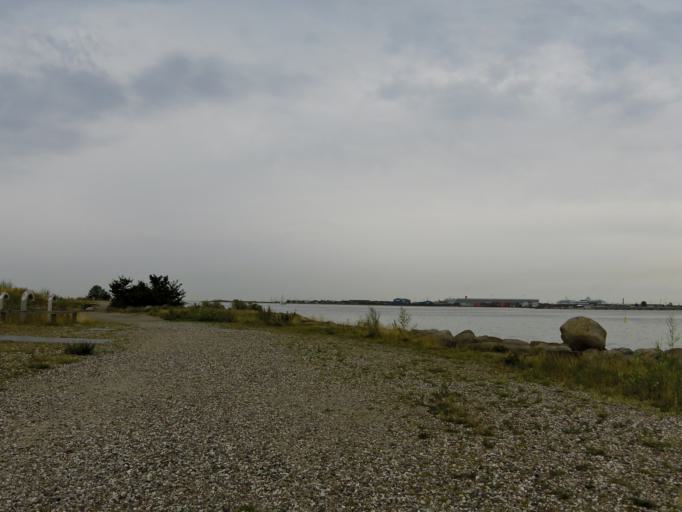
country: DK
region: Capital Region
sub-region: Gentofte Kommune
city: Charlottenlund
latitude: 55.7221
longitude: 12.5833
